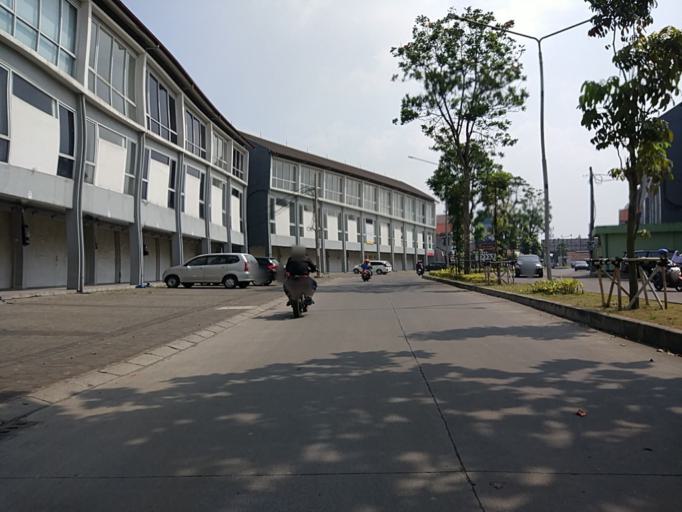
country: ID
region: West Java
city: Margahayukencana
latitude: -6.9378
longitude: 107.5716
